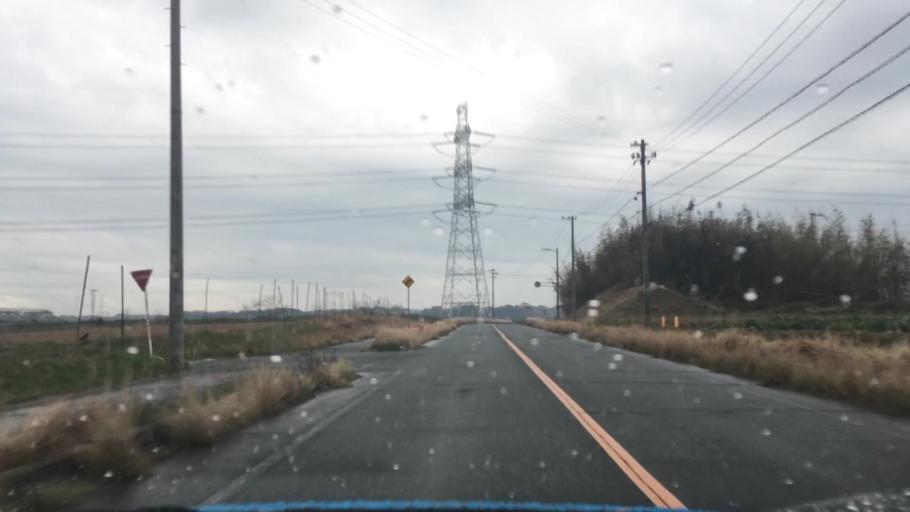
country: JP
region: Aichi
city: Toyohashi
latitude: 34.6763
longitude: 137.3907
